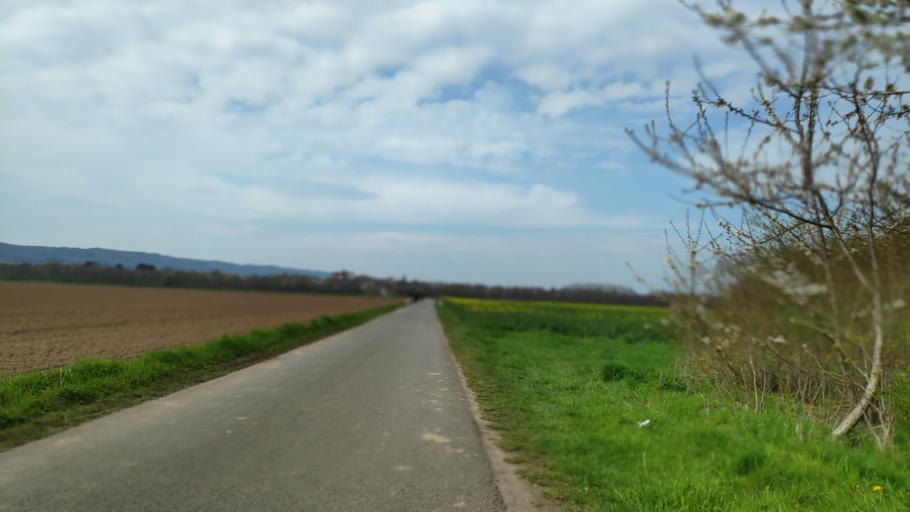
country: DE
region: North Rhine-Westphalia
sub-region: Regierungsbezirk Detmold
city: Minden
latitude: 52.2734
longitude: 8.9176
